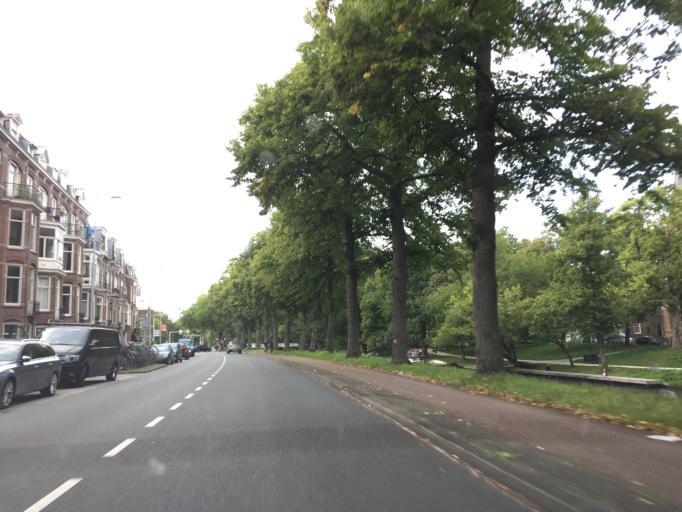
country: NL
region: Utrecht
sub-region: Gemeente Utrecht
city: Utrecht
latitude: 52.0836
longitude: 5.1199
